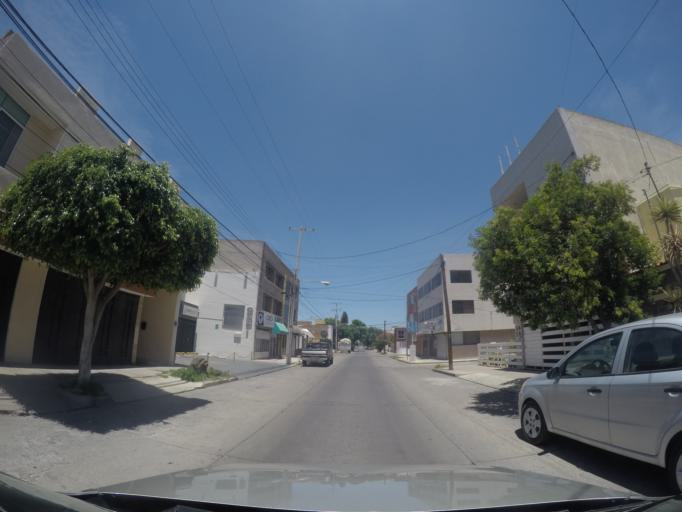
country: MX
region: San Luis Potosi
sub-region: San Luis Potosi
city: San Luis Potosi
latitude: 22.1506
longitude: -101.0092
